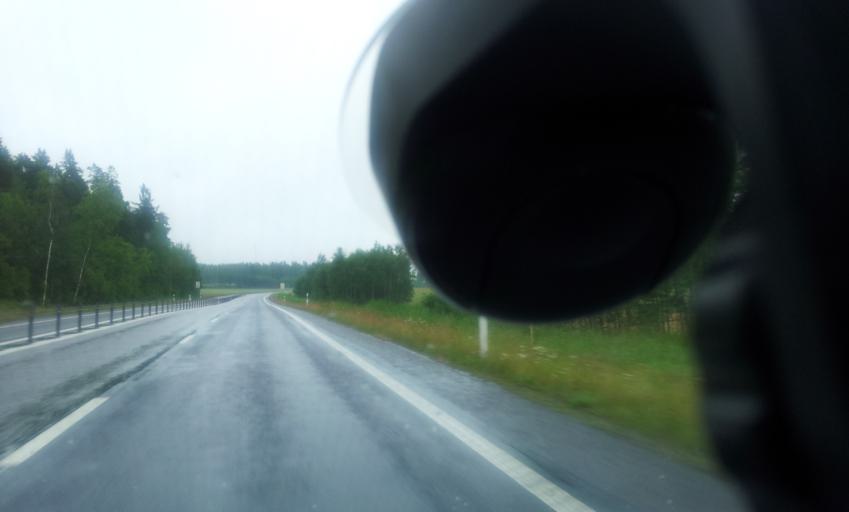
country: SE
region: OEstergoetland
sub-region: Soderkopings Kommun
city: Soederkoeping
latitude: 58.5057
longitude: 16.2962
